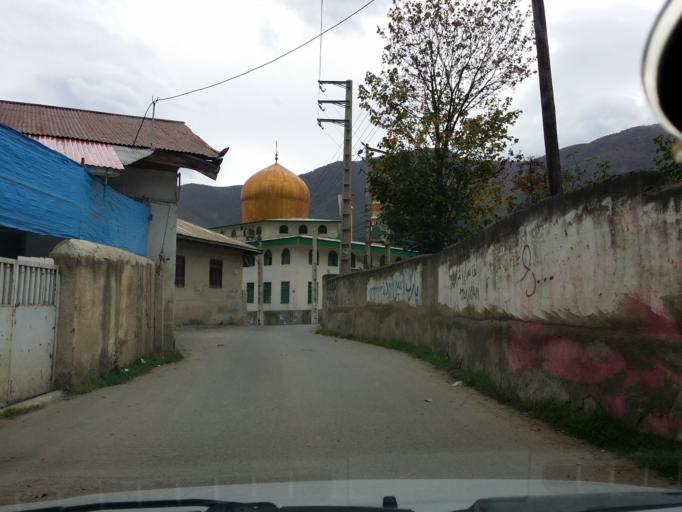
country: IR
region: Mazandaran
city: `Abbasabad
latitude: 36.5040
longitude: 51.1500
